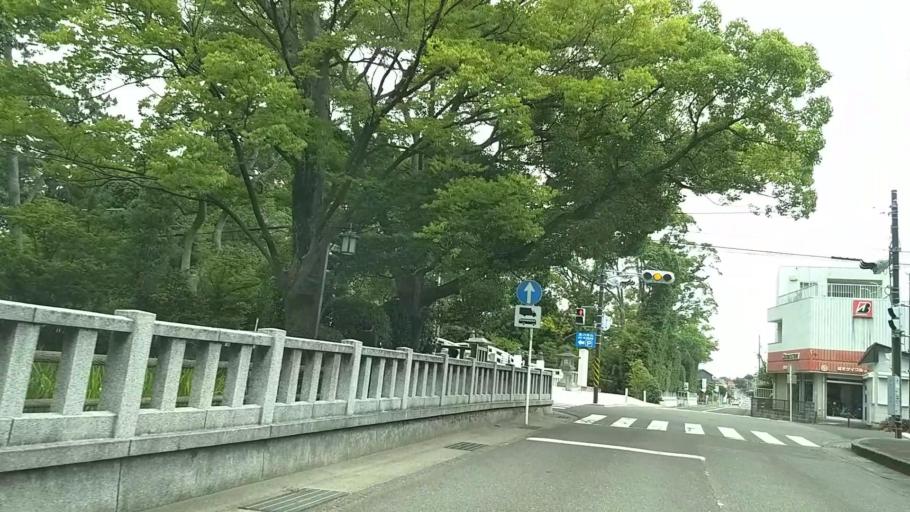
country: JP
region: Kanagawa
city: Chigasaki
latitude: 35.3781
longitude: 139.3814
